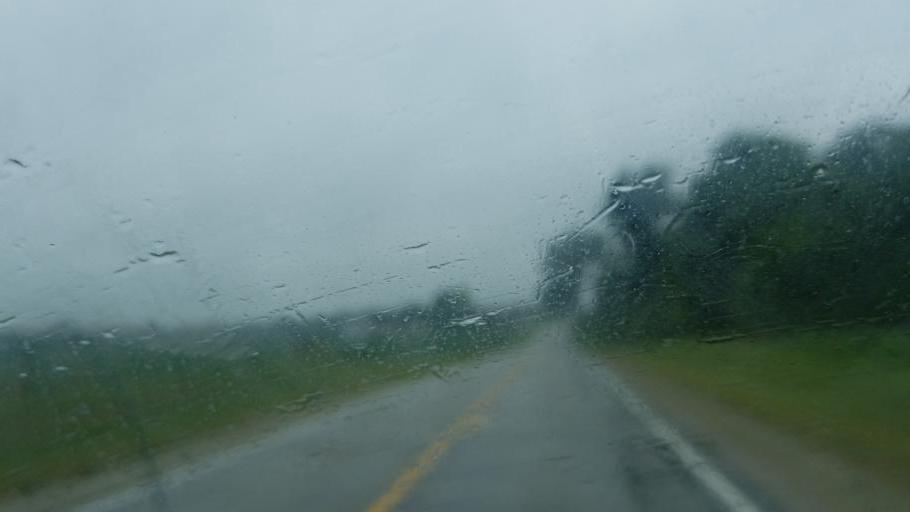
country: US
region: Indiana
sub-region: Huntington County
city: Warren
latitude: 40.6574
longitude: -85.4008
